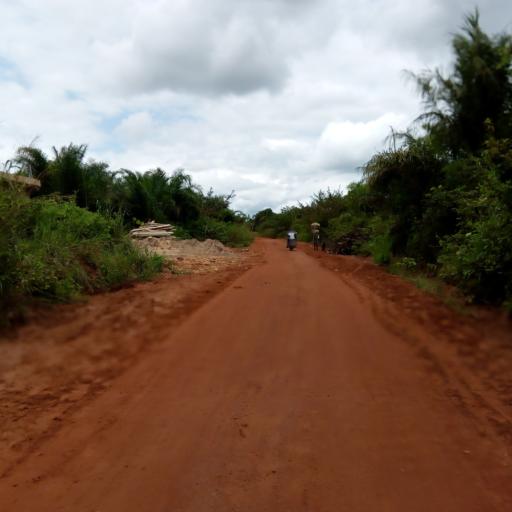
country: TG
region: Maritime
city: Tsevie
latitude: 6.3388
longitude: 1.0971
